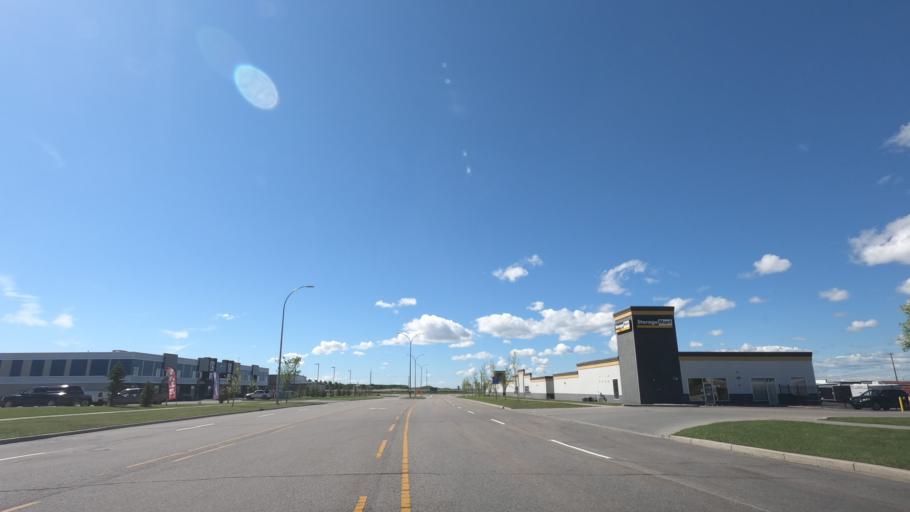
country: CA
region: Alberta
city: Airdrie
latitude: 51.2585
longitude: -113.9951
